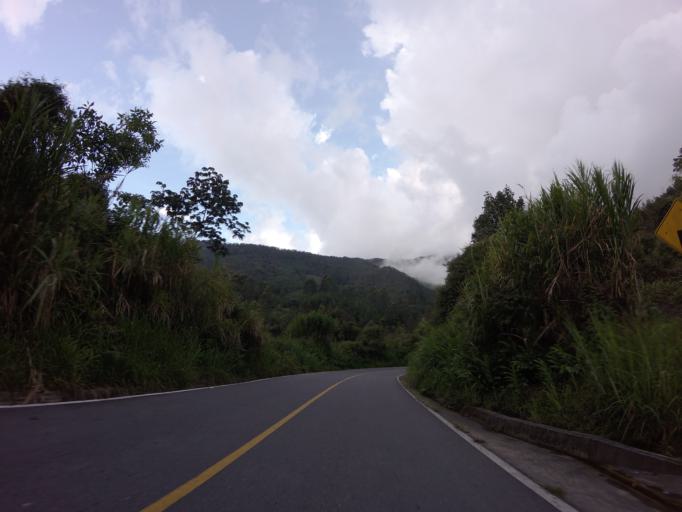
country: CO
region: Caldas
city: Pensilvania
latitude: 5.3763
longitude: -75.1496
